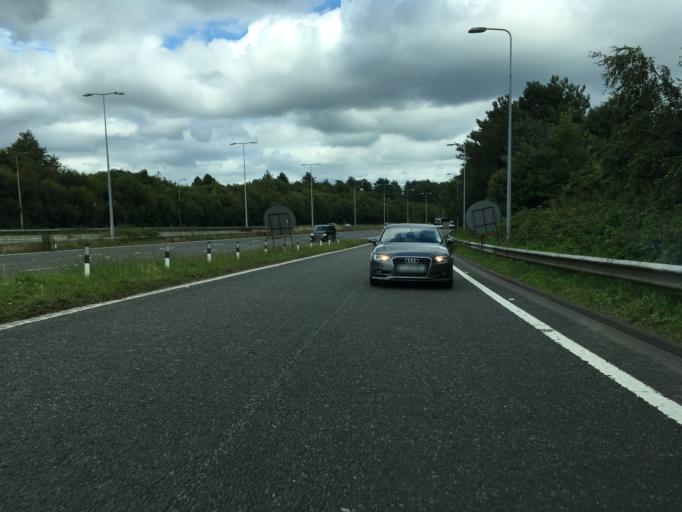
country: GB
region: England
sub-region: West Sussex
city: Broadfield
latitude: 51.0877
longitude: -0.1920
